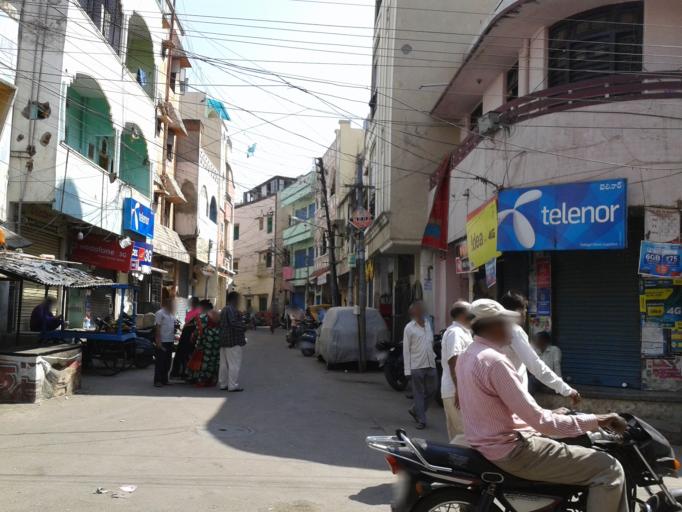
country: IN
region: Telangana
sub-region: Hyderabad
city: Malkajgiri
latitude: 17.4371
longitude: 78.4966
